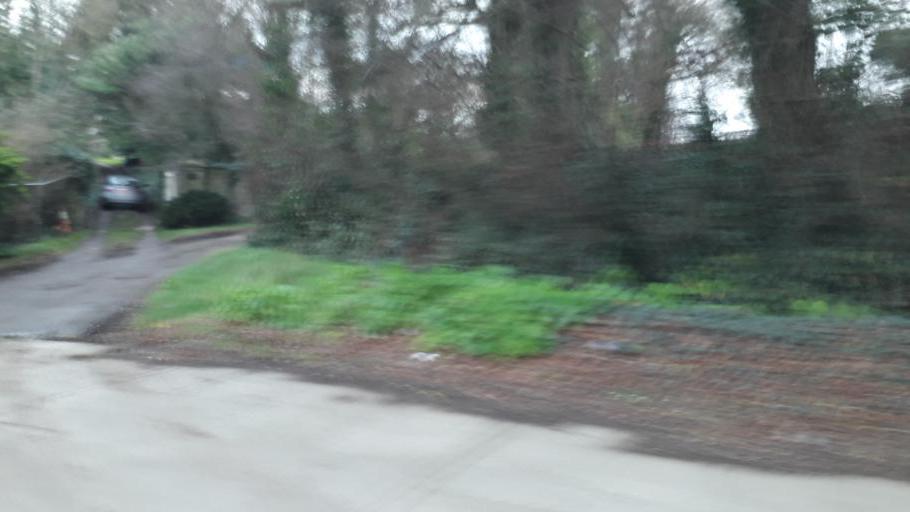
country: IE
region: Leinster
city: An Ros
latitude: 53.5182
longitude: -6.1256
